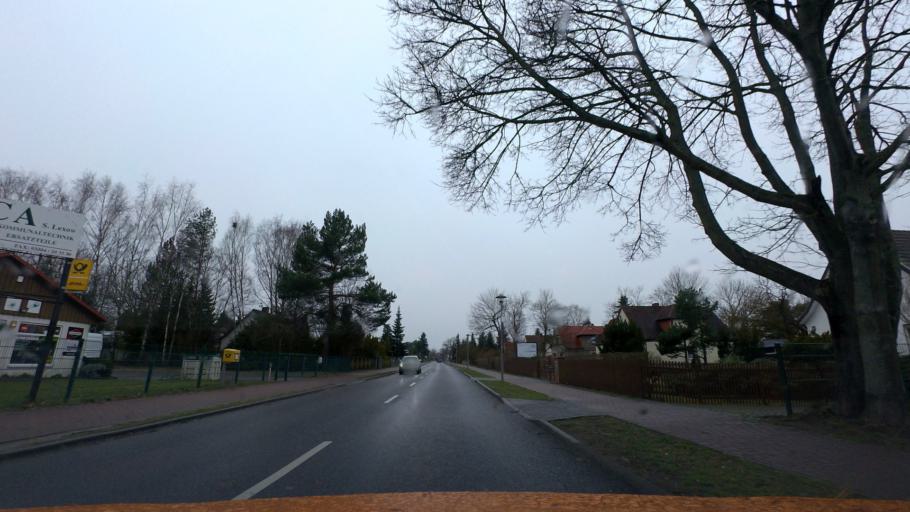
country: DE
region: Brandenburg
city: Velten
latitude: 52.6564
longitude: 13.1458
